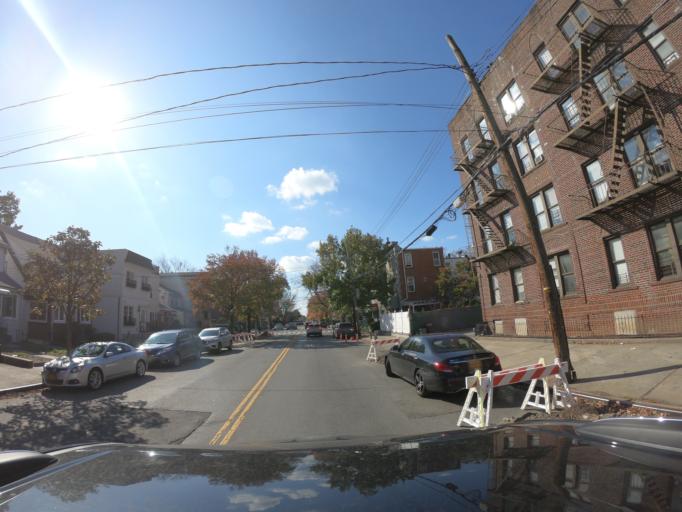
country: US
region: New York
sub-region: Kings County
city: Bensonhurst
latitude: 40.6243
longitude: -73.9778
